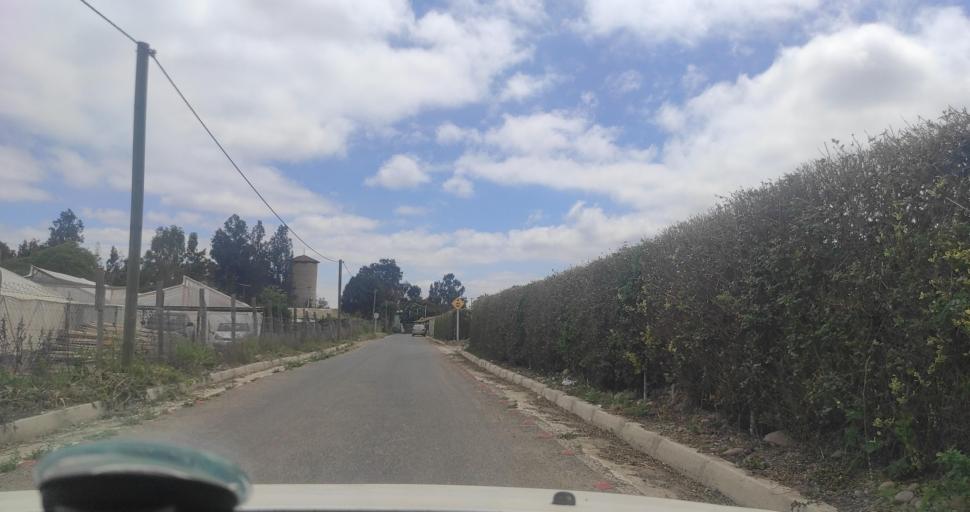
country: CL
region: Valparaiso
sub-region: Provincia de Marga Marga
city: Limache
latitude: -33.0166
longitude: -71.2412
